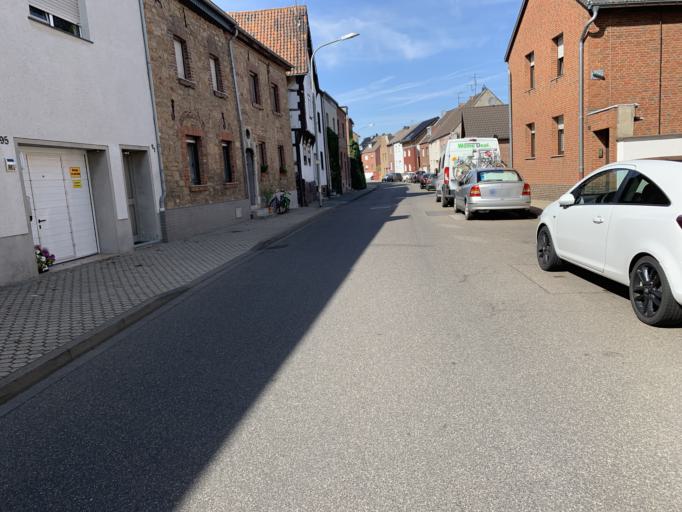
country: DE
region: North Rhine-Westphalia
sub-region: Regierungsbezirk Koln
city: Dueren
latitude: 50.8002
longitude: 6.4320
